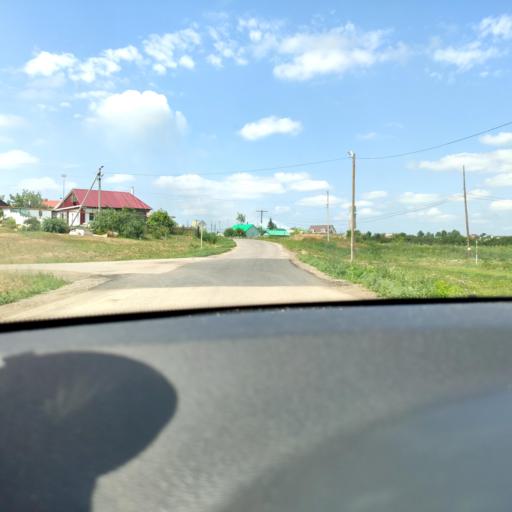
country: RU
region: Samara
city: Kinel'
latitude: 53.3399
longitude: 50.5258
